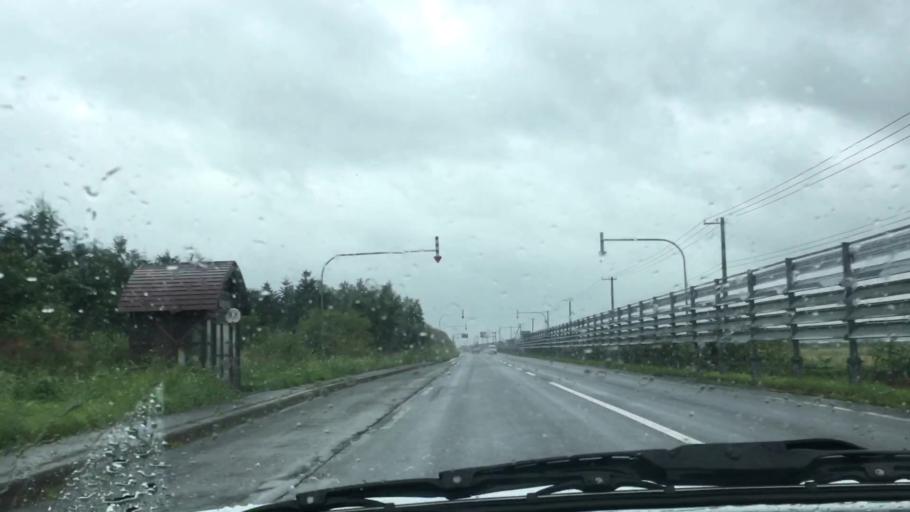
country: JP
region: Hokkaido
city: Nanae
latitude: 42.3079
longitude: 140.2726
